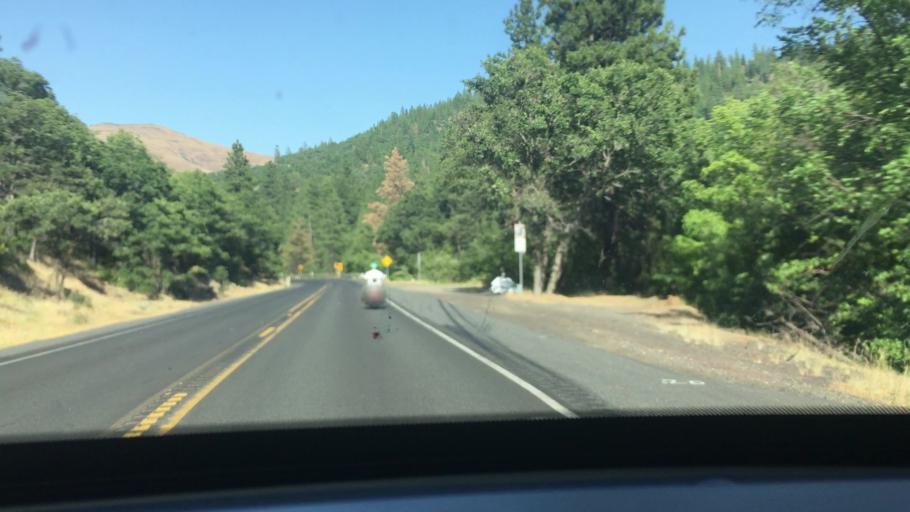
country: US
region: Washington
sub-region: Klickitat County
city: Goldendale
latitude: 46.0382
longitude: -120.5792
